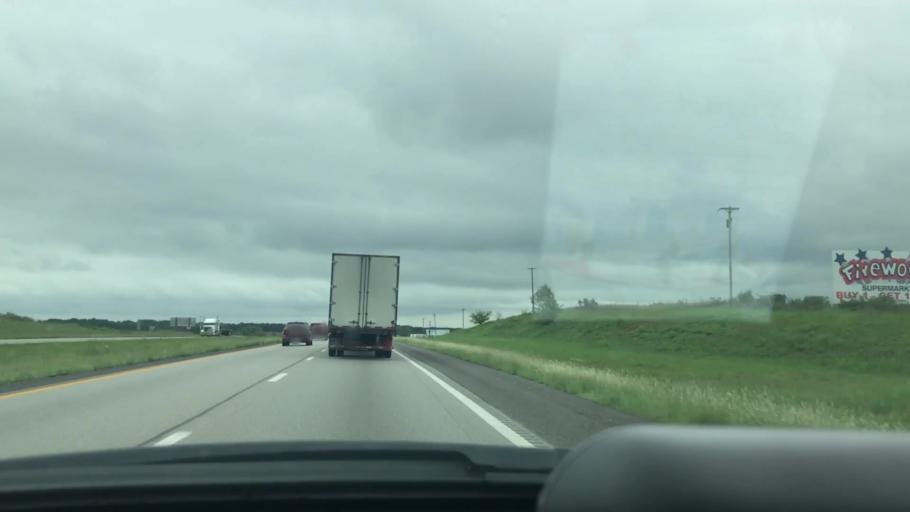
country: US
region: Missouri
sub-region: Christian County
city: Billings
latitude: 37.1856
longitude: -93.5922
